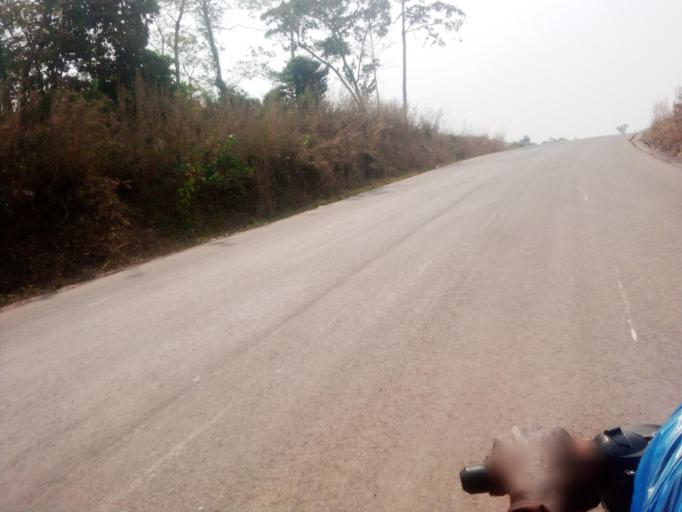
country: SL
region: Southern Province
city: Bo
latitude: 7.9241
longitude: -11.7692
